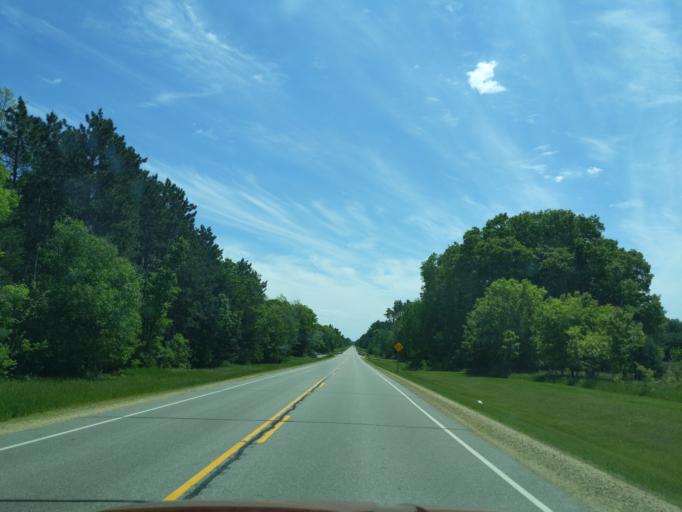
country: US
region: Wisconsin
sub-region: Marquette County
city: Montello
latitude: 43.9186
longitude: -89.3122
